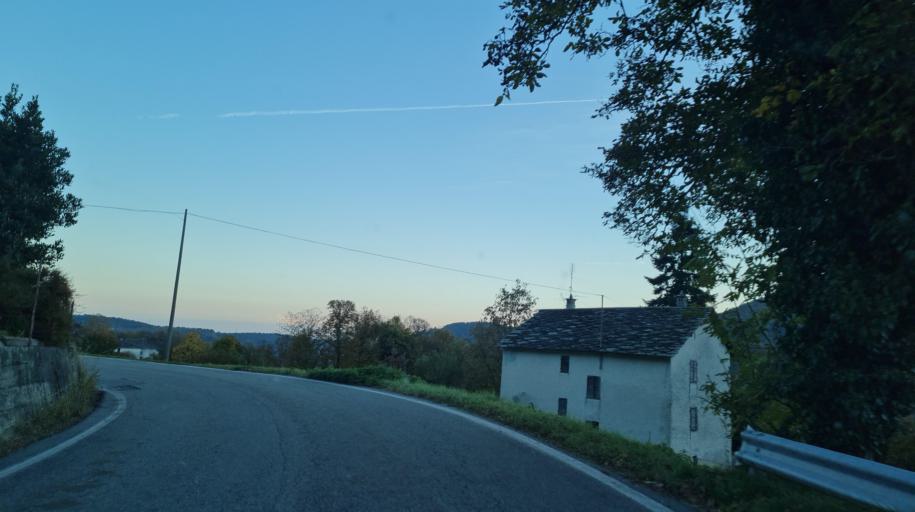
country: IT
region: Piedmont
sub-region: Provincia di Torino
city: Trausella
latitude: 45.4991
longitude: 7.7628
